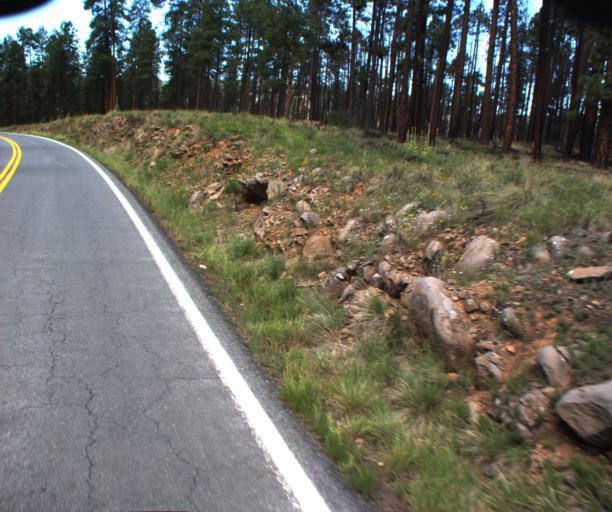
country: US
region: Arizona
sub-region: Apache County
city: Eagar
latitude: 33.7630
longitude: -109.2084
